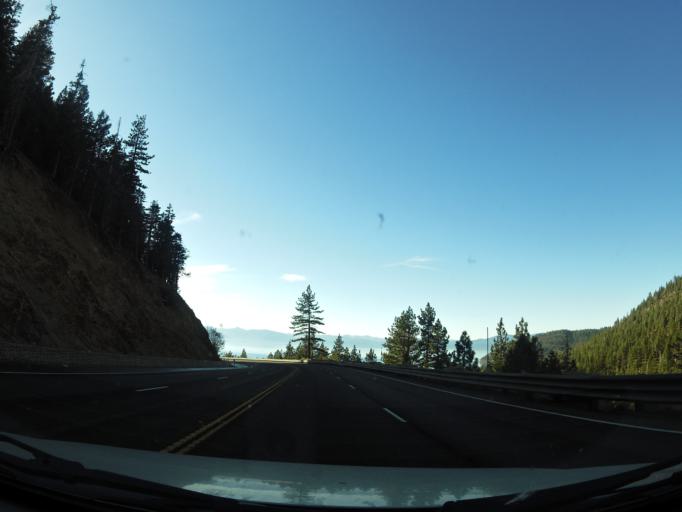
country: US
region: Nevada
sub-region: Douglas County
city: Kingsbury
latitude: 39.0854
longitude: -119.9258
